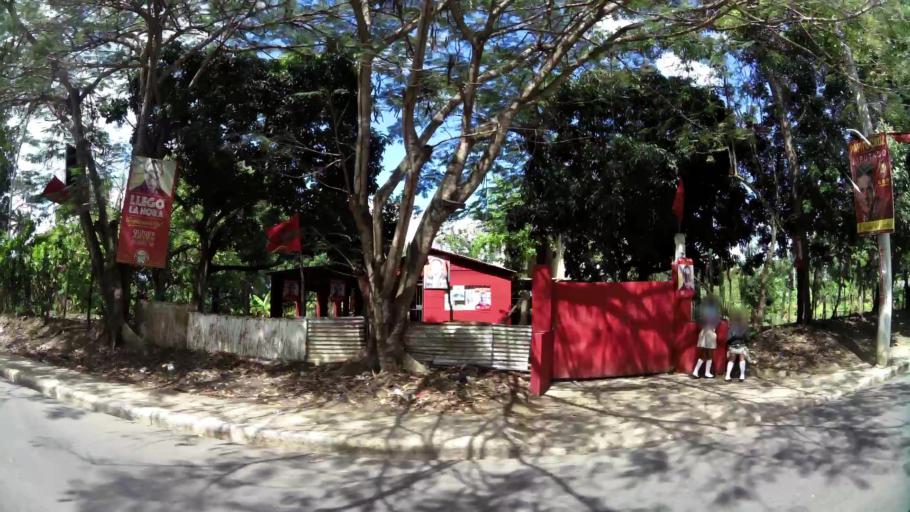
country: DO
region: Santiago
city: Licey al Medio
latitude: 19.3877
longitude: -70.6332
